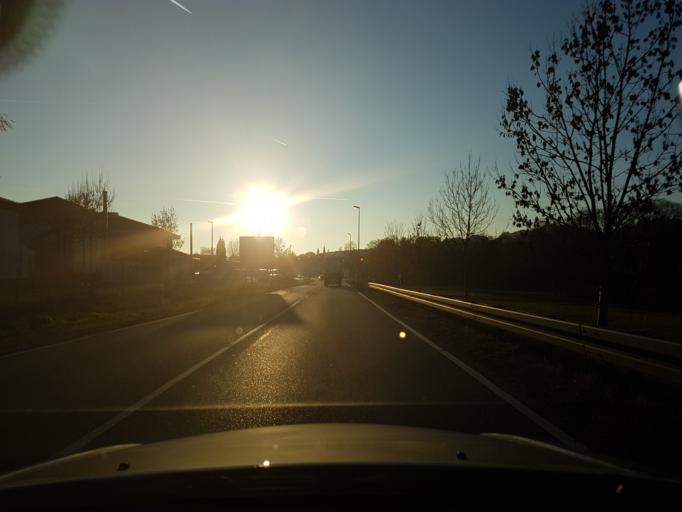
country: DE
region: Hesse
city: Taunusstein
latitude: 50.1723
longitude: 8.2143
